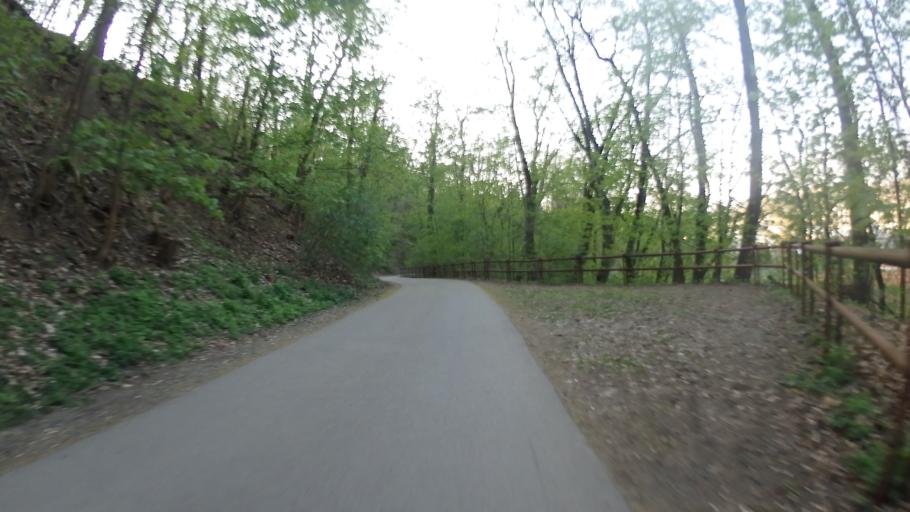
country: CZ
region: South Moravian
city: Moravany
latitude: 49.1826
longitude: 16.5740
